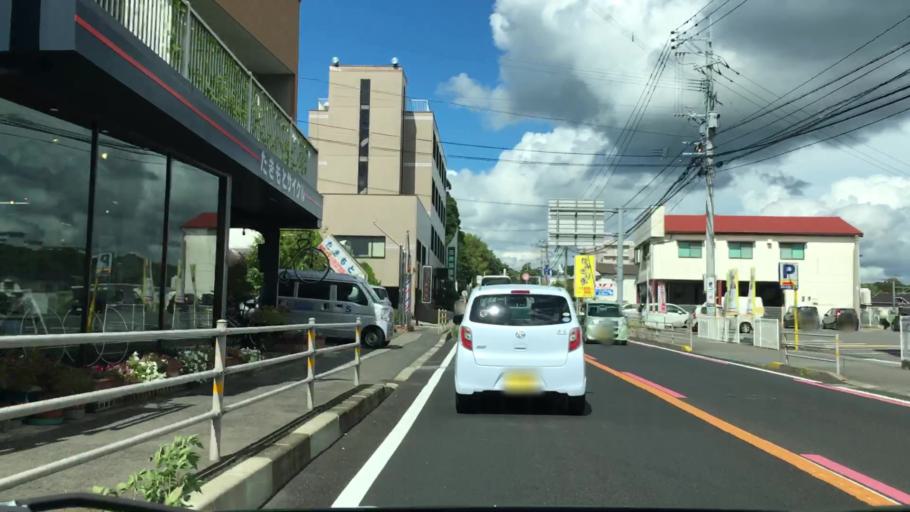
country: JP
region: Nagasaki
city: Sasebo
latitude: 33.1425
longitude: 129.8000
